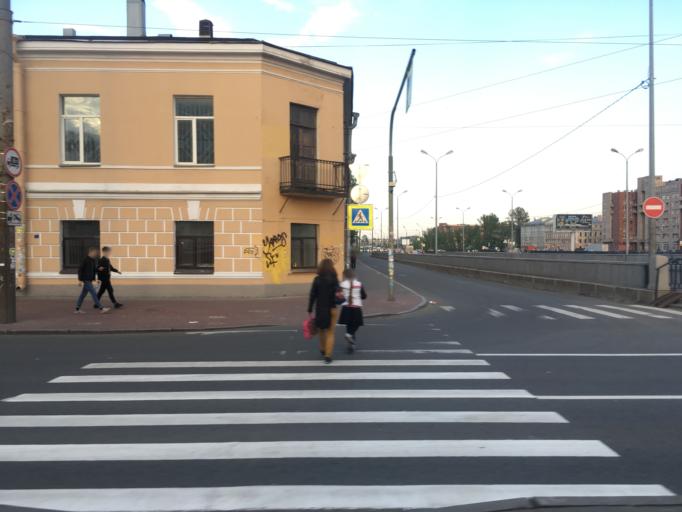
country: RU
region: St.-Petersburg
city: Centralniy
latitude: 59.9158
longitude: 30.3513
